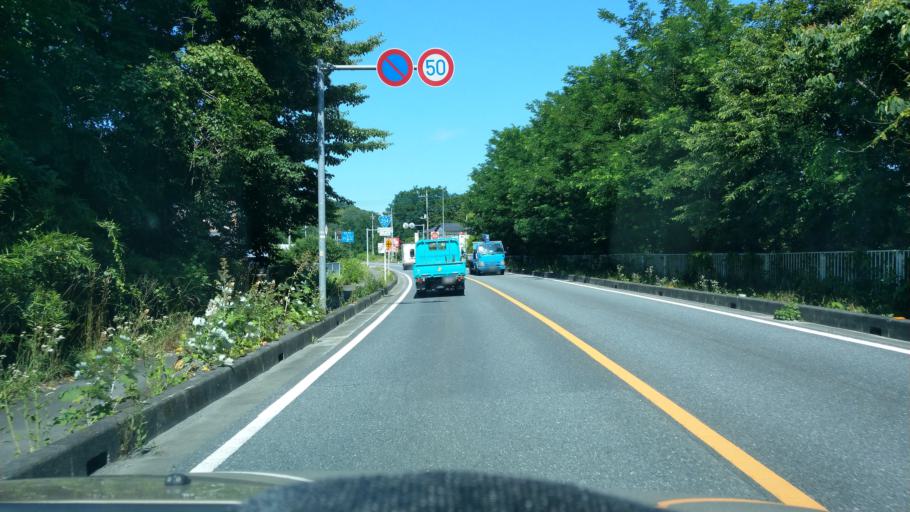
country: JP
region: Saitama
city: Ogawa
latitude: 36.0703
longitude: 139.2811
